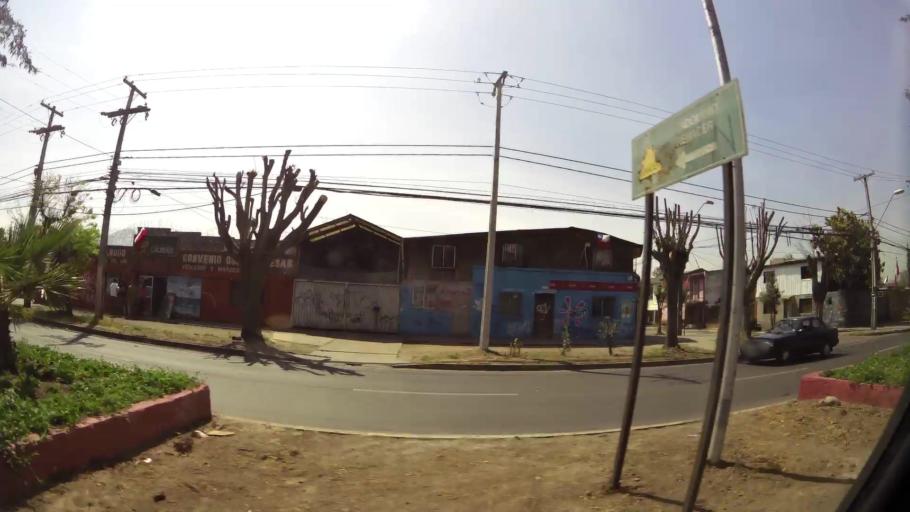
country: CL
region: Santiago Metropolitan
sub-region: Provincia de Santiago
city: Lo Prado
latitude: -33.4200
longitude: -70.7047
